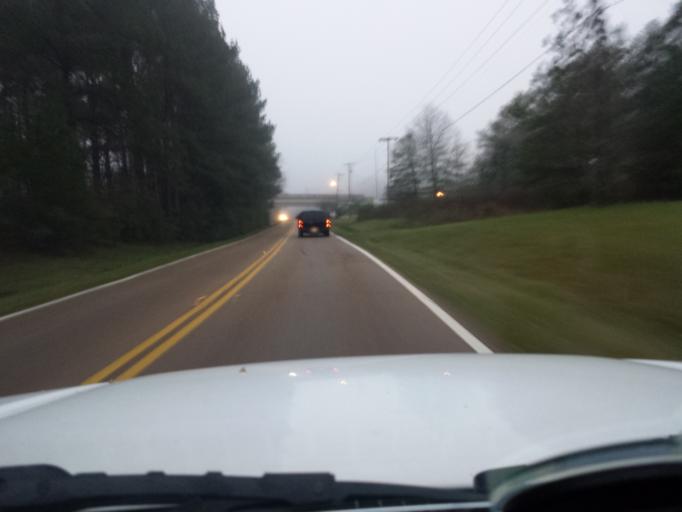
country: US
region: Mississippi
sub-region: Rankin County
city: Flowood
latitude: 32.3406
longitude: -90.0780
